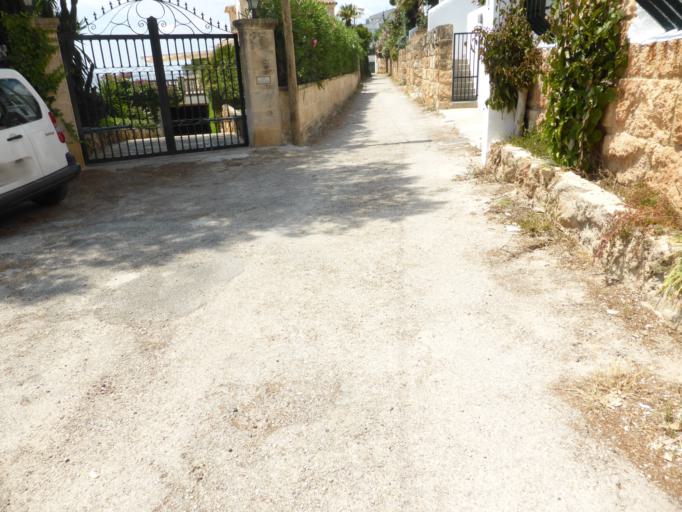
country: ES
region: Balearic Islands
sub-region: Illes Balears
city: Port d'Alcudia
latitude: 39.8378
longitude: 3.1571
